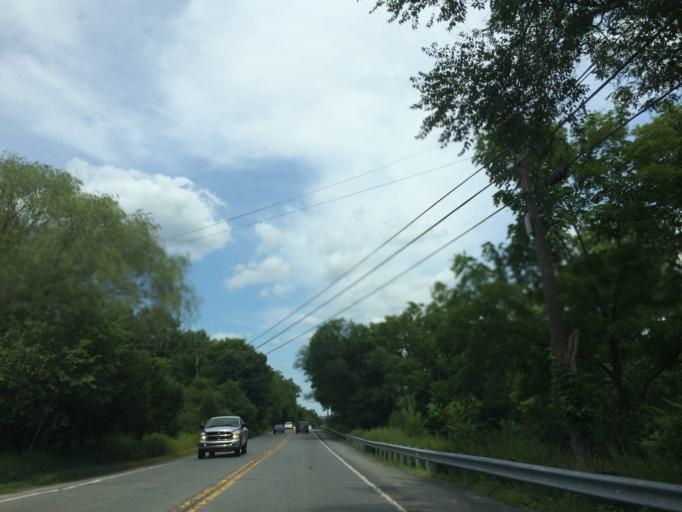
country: US
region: Pennsylvania
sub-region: Pike County
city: Saw Creek
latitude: 41.0667
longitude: -75.0514
